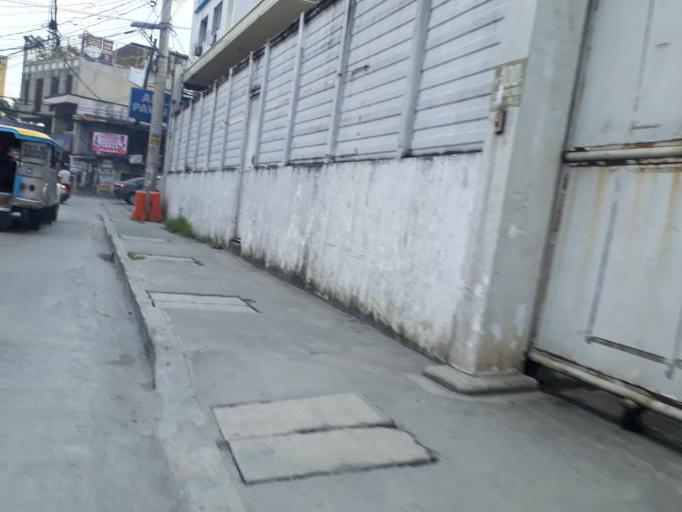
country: PH
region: Metro Manila
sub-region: Caloocan City
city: Niugan
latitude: 14.6604
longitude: 120.9571
